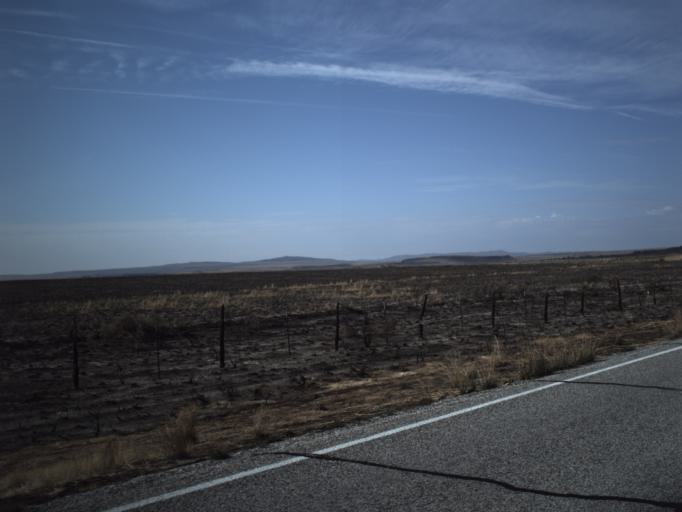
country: US
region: Idaho
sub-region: Minidoka County
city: Rupert
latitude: 41.8281
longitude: -113.1687
